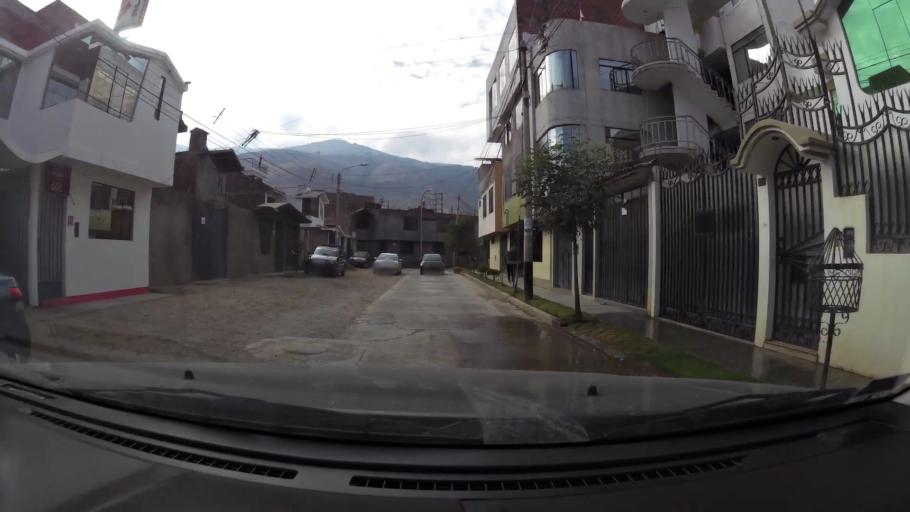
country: PE
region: Junin
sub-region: Provincia de Huancayo
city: Huancayo
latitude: -12.0487
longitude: -75.1933
